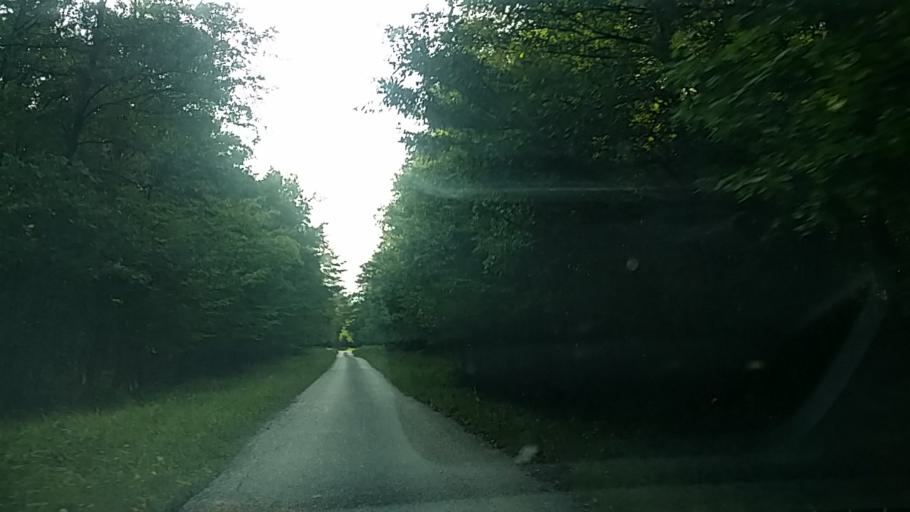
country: HU
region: Komarom-Esztergom
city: Tatabanya
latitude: 47.5928
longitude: 18.4224
